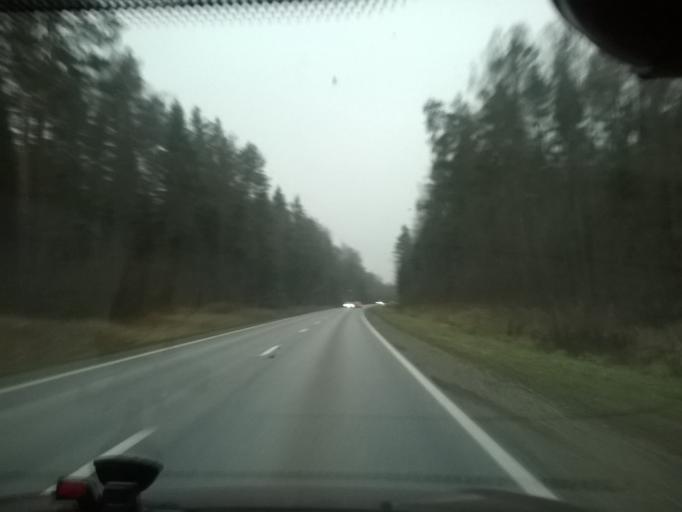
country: LV
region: Pargaujas
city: Stalbe
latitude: 57.3804
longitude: 25.0634
